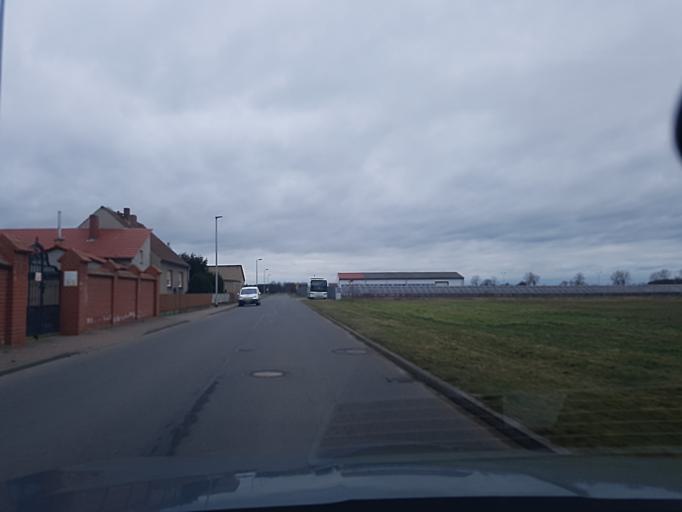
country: DE
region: Brandenburg
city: Falkenberg
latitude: 51.5953
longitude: 13.2943
